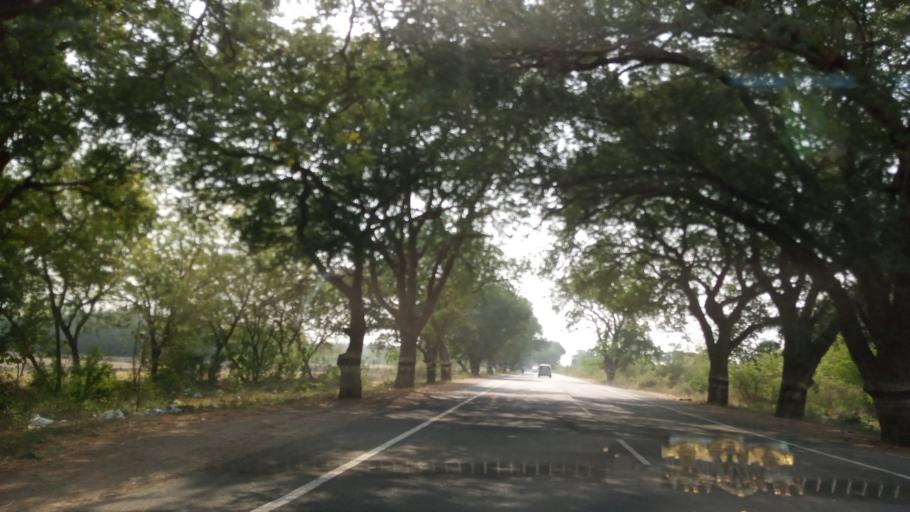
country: IN
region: Tamil Nadu
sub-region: Cuddalore
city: Pennadam
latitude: 11.5362
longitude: 79.1692
